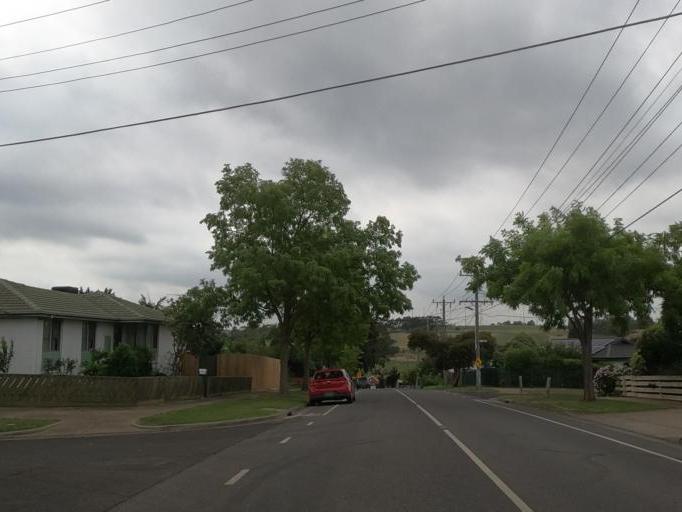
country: AU
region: Victoria
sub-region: Hume
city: Broadmeadows
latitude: -37.6721
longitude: 144.9093
